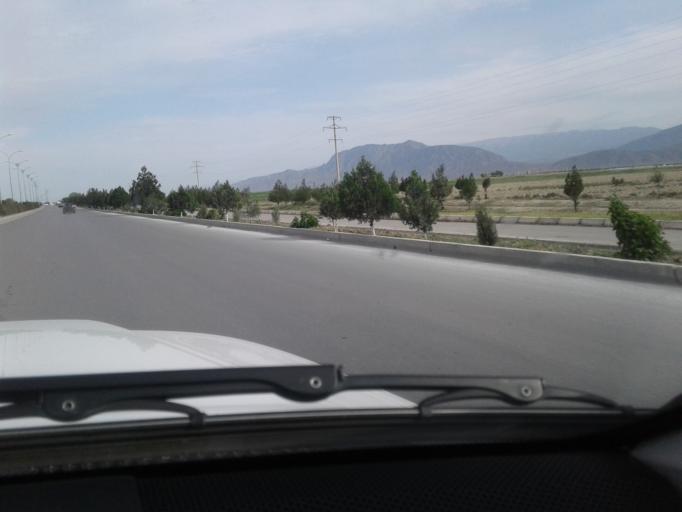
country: TM
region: Ahal
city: Abadan
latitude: 38.1527
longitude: 57.9784
